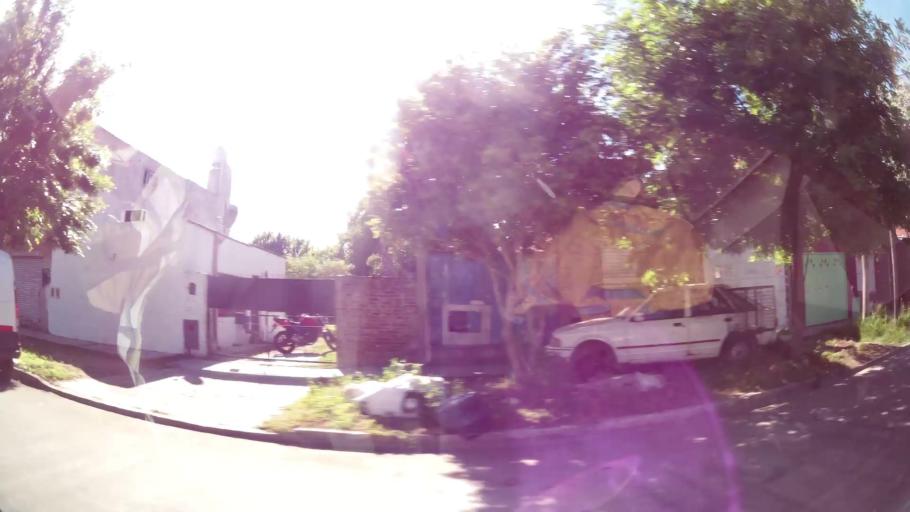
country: AR
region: Buenos Aires
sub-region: Partido de Tigre
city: Tigre
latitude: -34.4773
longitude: -58.5800
